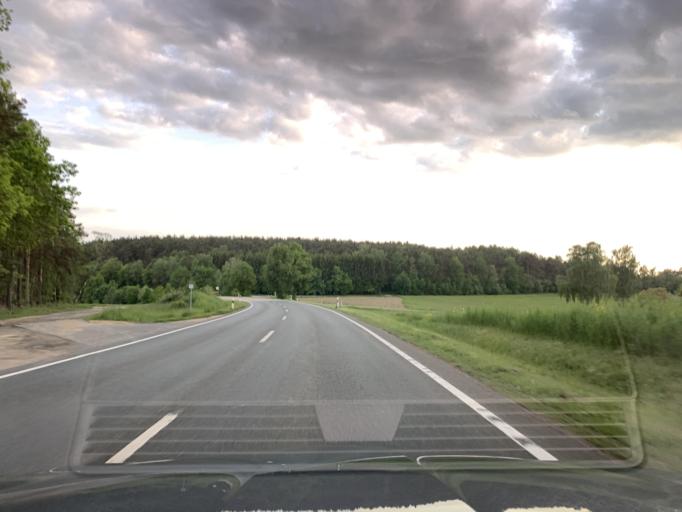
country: DE
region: Bavaria
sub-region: Upper Palatinate
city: Pettendorf
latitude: 49.3300
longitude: 12.3359
